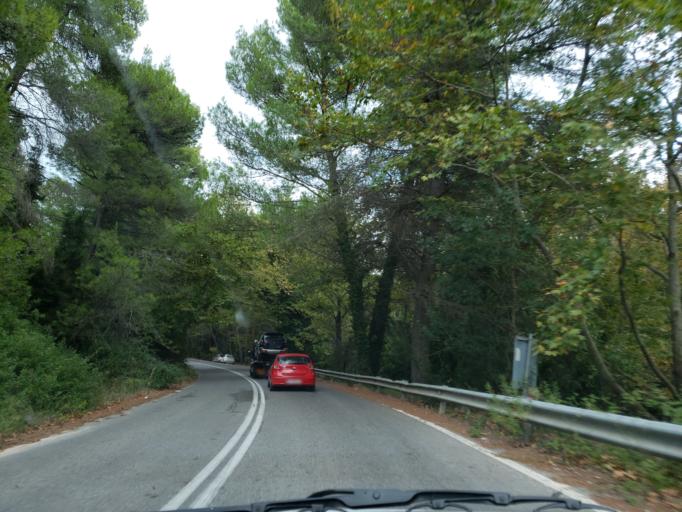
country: GR
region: Attica
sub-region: Nomarchia Anatolikis Attikis
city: Varnavas
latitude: 38.2107
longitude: 23.9034
